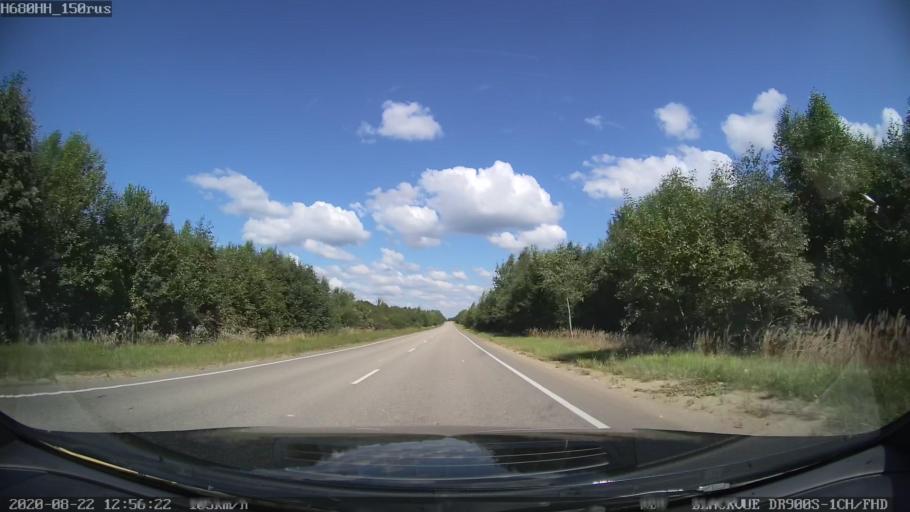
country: RU
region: Tverskaya
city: Rameshki
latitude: 57.5553
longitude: 36.3157
